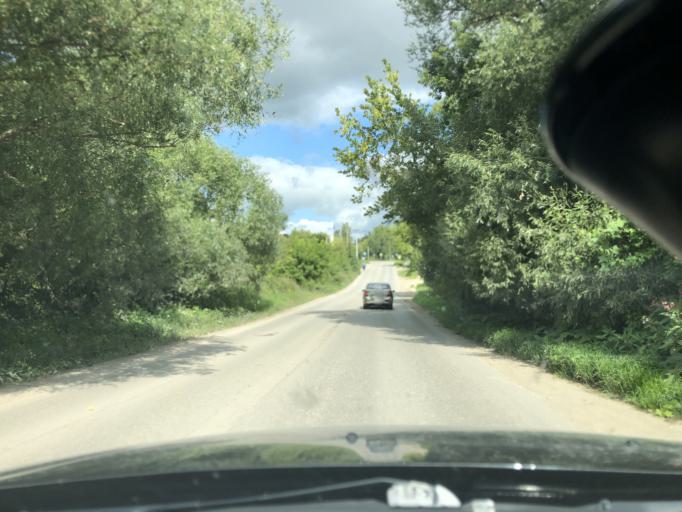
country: RU
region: Tula
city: Yasnogorsk
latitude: 54.4665
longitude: 37.7018
